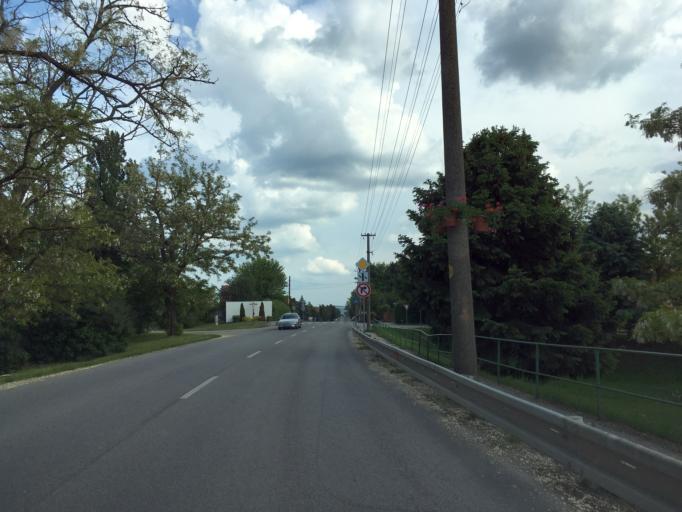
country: HU
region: Komarom-Esztergom
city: Dunaalmas
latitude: 47.7888
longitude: 18.2911
